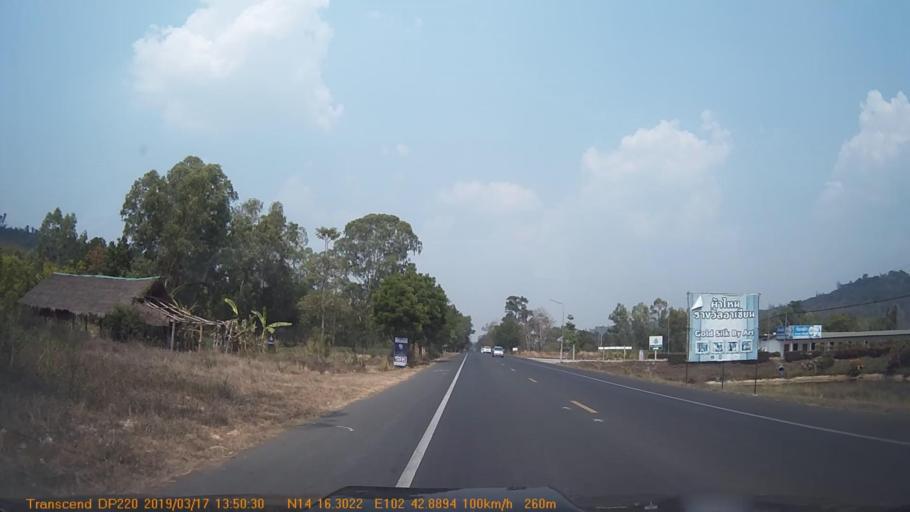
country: TH
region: Buriram
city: Non Din Daeng
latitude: 14.2719
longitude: 102.7151
